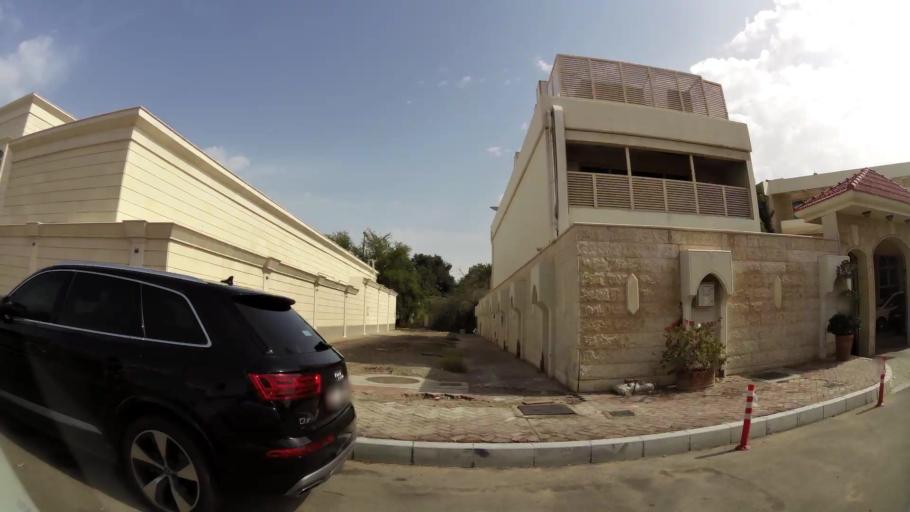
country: AE
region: Abu Dhabi
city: Abu Dhabi
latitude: 24.4438
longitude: 54.3597
